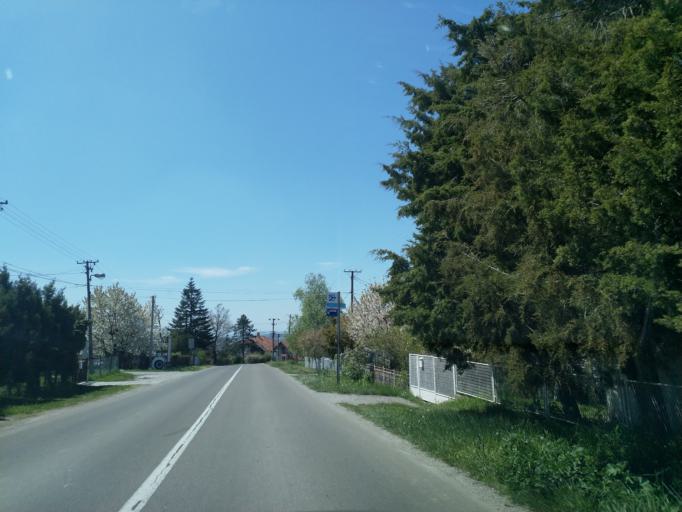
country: RS
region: Central Serbia
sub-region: Belgrade
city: Lazarevac
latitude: 44.3720
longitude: 20.3062
